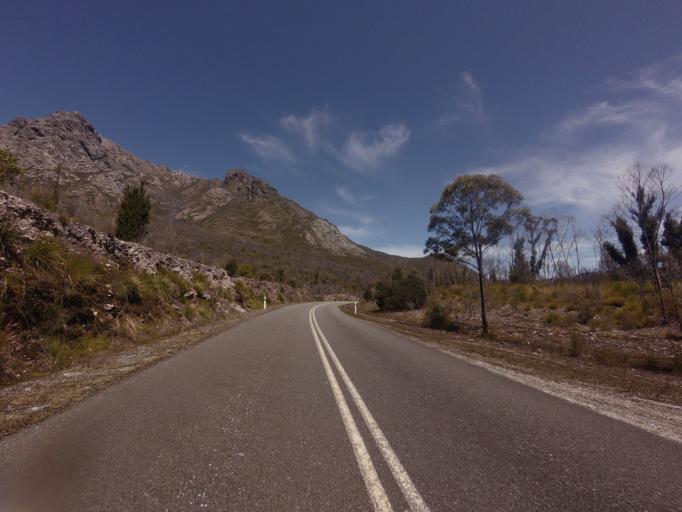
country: AU
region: Tasmania
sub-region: Huon Valley
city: Geeveston
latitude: -42.8598
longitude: 146.2287
